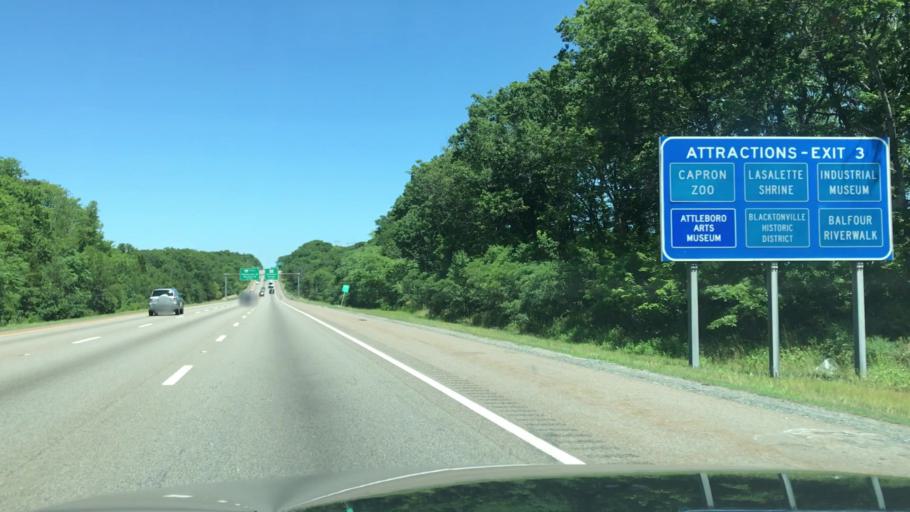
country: US
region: Massachusetts
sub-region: Bristol County
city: North Seekonk
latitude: 41.9237
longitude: -71.3272
